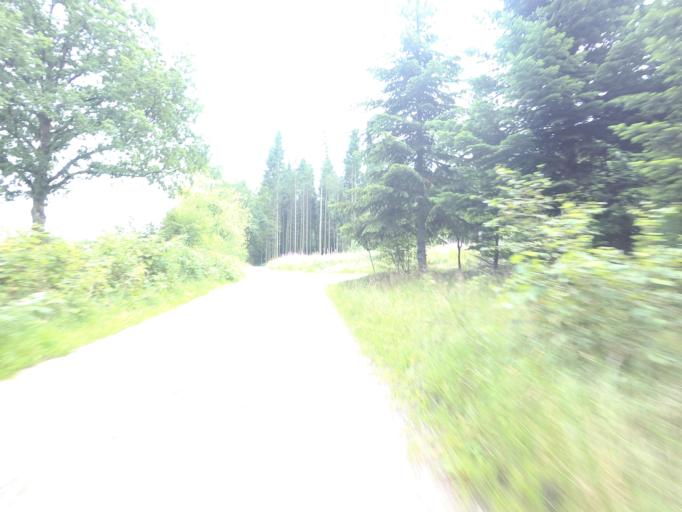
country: DK
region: Central Jutland
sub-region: Silkeborg Kommune
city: Virklund
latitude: 56.0239
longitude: 9.4964
